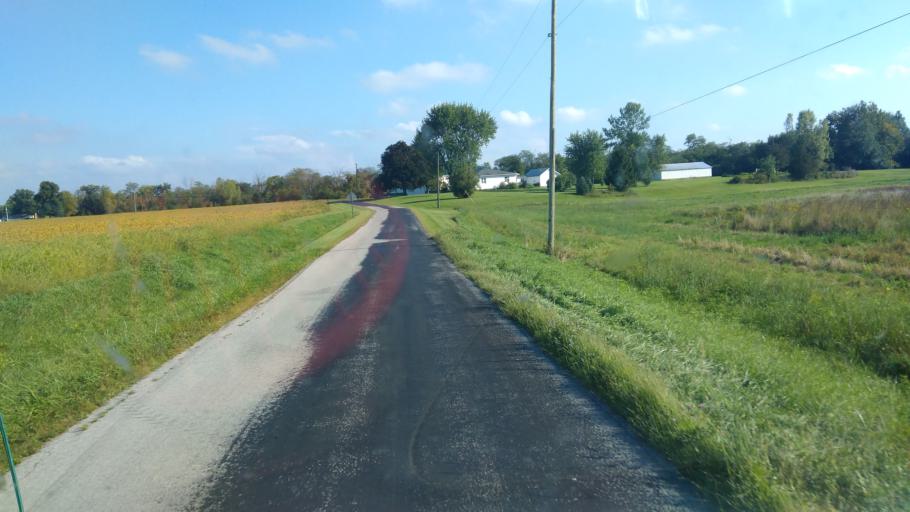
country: US
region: Ohio
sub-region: Hardin County
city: Forest
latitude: 40.7200
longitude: -83.4594
